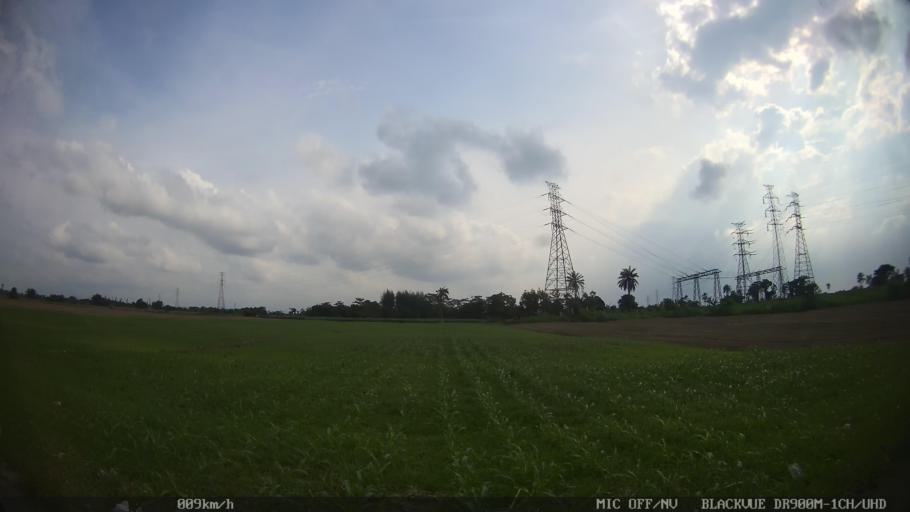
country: ID
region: North Sumatra
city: Percut
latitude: 3.5658
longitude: 98.7832
